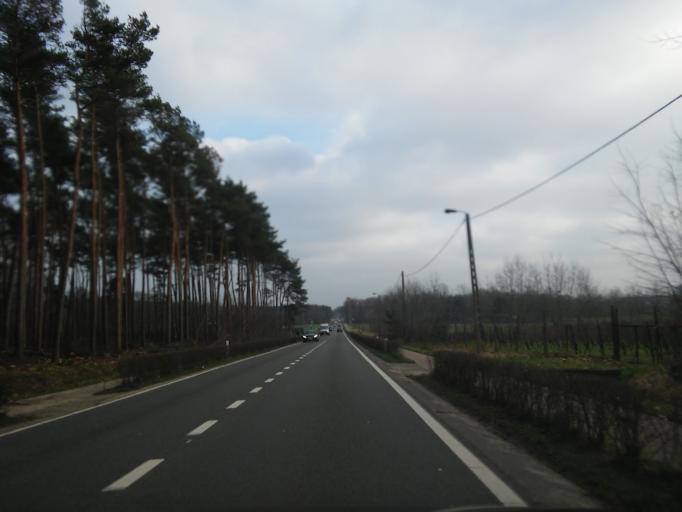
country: BE
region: Flanders
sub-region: Provincie Antwerpen
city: Herselt
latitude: 51.0489
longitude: 4.8996
